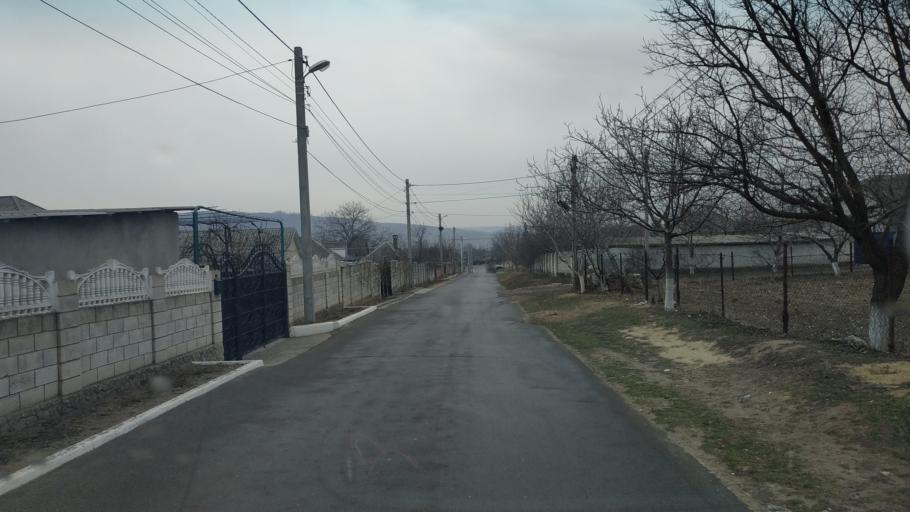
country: MD
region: Chisinau
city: Singera
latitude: 46.9187
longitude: 28.9593
